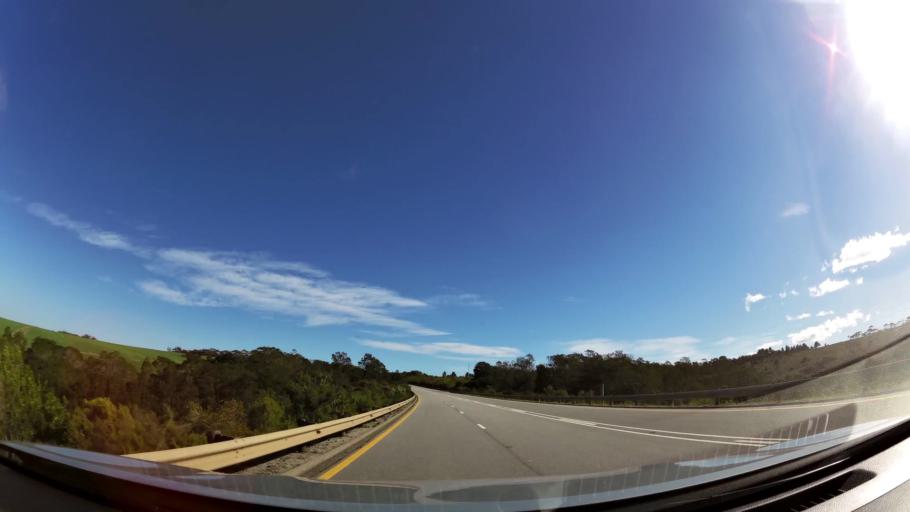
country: ZA
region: Eastern Cape
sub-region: Cacadu District Municipality
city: Kruisfontein
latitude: -34.0163
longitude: 24.6266
